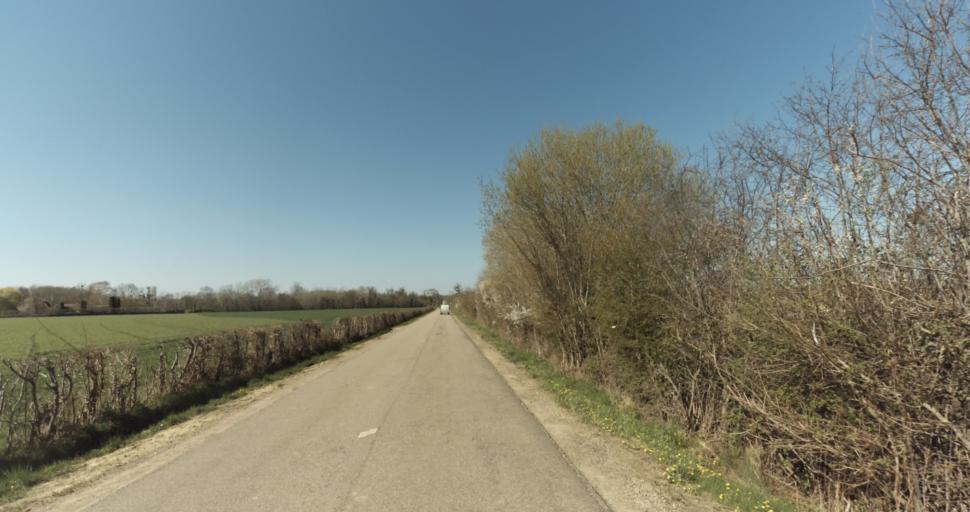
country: FR
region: Lower Normandy
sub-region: Departement du Calvados
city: Saint-Pierre-sur-Dives
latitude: 48.9948
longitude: 0.0153
